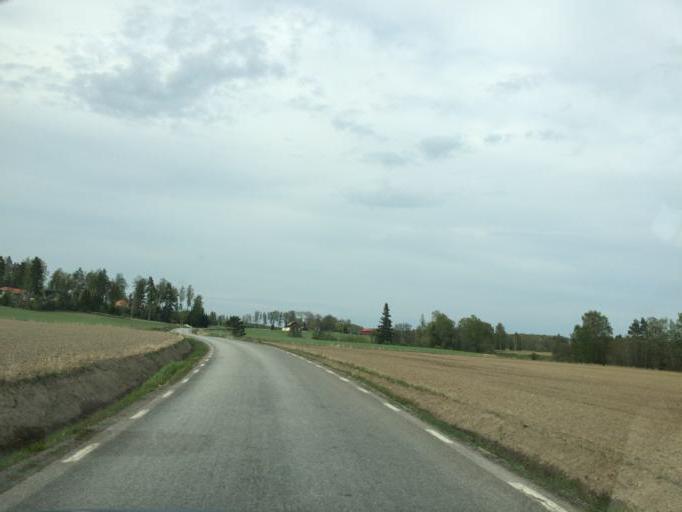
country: SE
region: Vaestmanland
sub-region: Kopings Kommun
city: Koping
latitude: 59.5907
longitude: 15.9927
